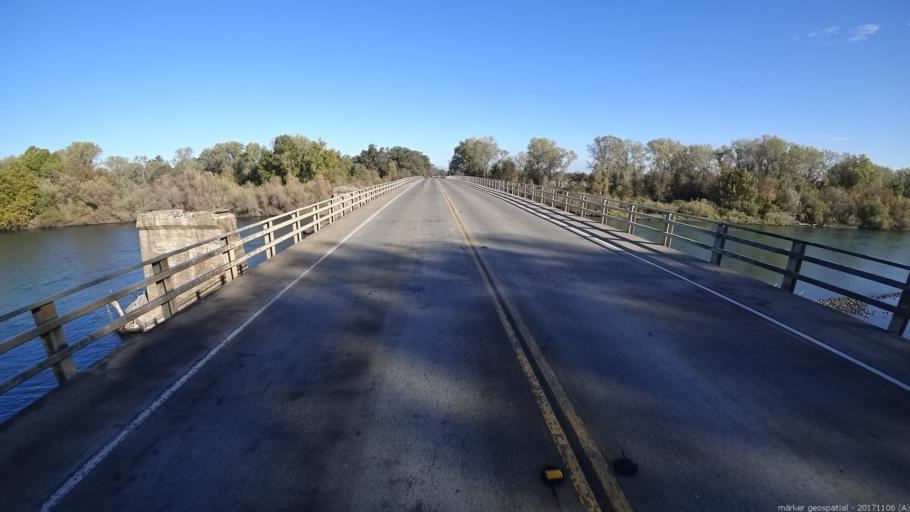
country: US
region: California
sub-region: Shasta County
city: Anderson
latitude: 40.4622
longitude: -122.2439
